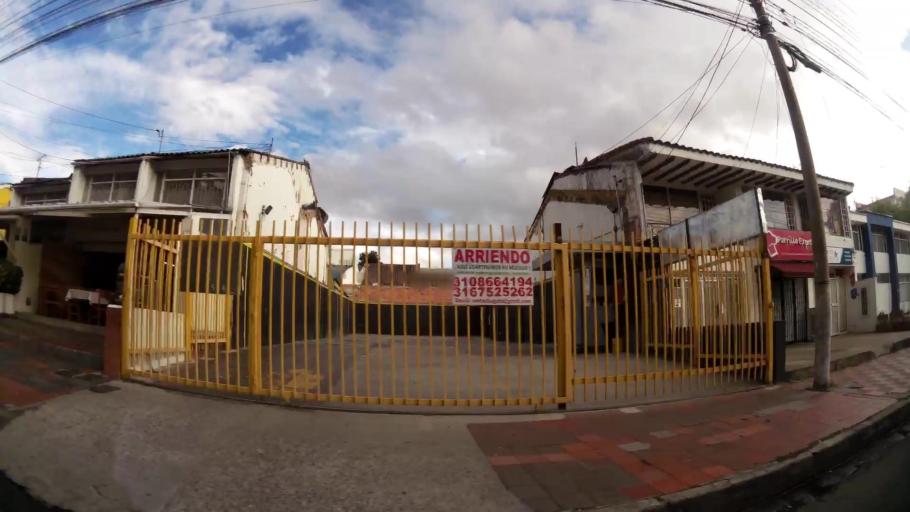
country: CO
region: Bogota D.C.
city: Barrio San Luis
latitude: 4.6987
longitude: -74.0722
